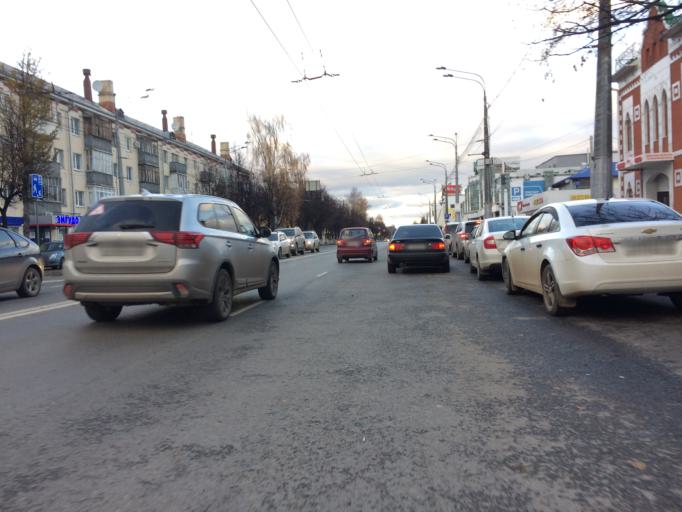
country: RU
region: Mariy-El
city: Yoshkar-Ola
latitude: 56.6324
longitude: 47.8833
